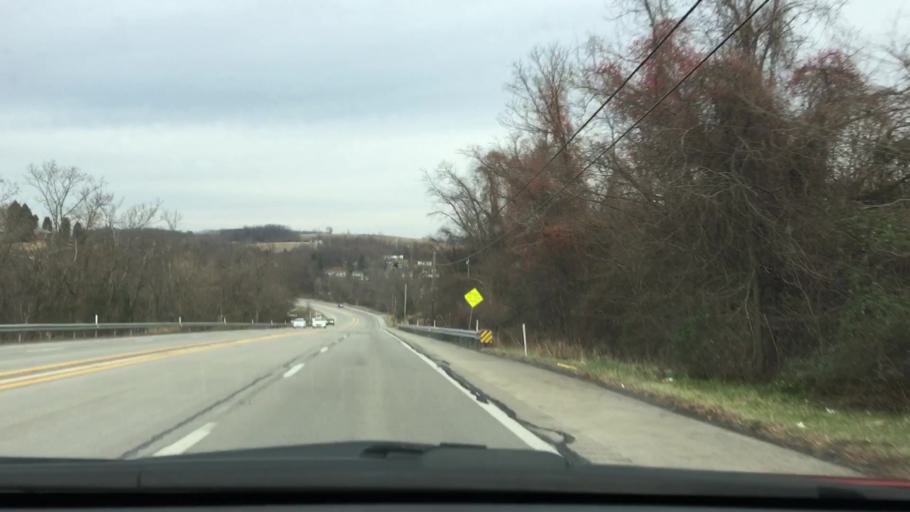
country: US
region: Pennsylvania
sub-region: Fayette County
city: Perryopolis
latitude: 40.1159
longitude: -79.7721
